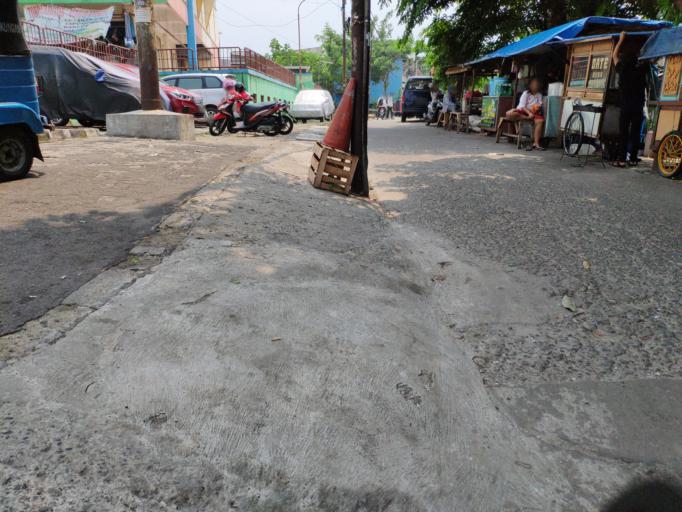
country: ID
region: Jakarta Raya
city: Jakarta
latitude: -6.2052
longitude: 106.8604
